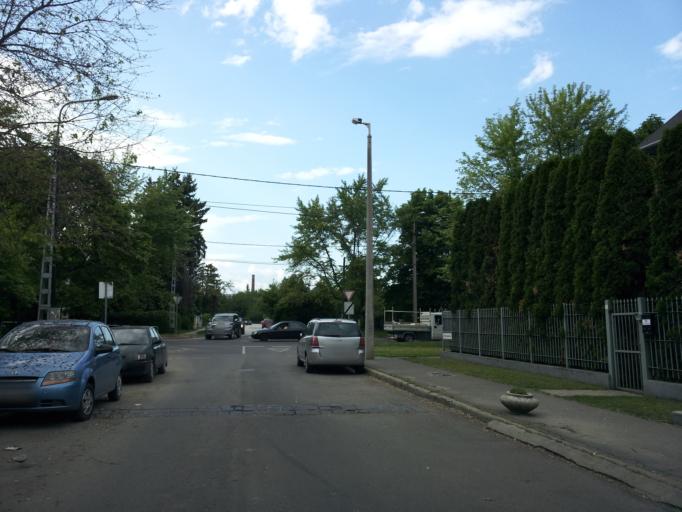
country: HU
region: Budapest
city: Budapest III. keruelet
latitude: 47.5596
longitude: 19.0273
